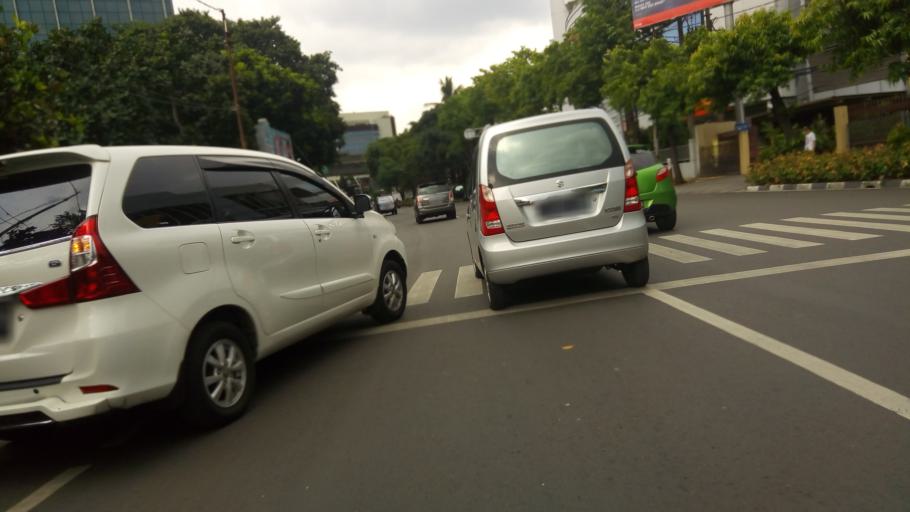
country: ID
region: Jakarta Raya
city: Jakarta
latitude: -6.2459
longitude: 106.8031
